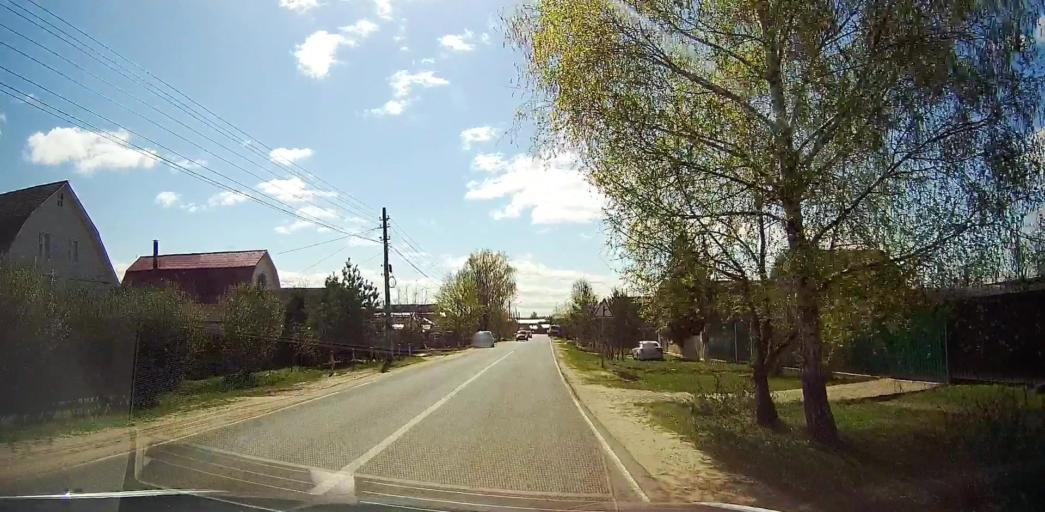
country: RU
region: Moskovskaya
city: Ramenskoye
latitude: 55.6182
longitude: 38.3033
